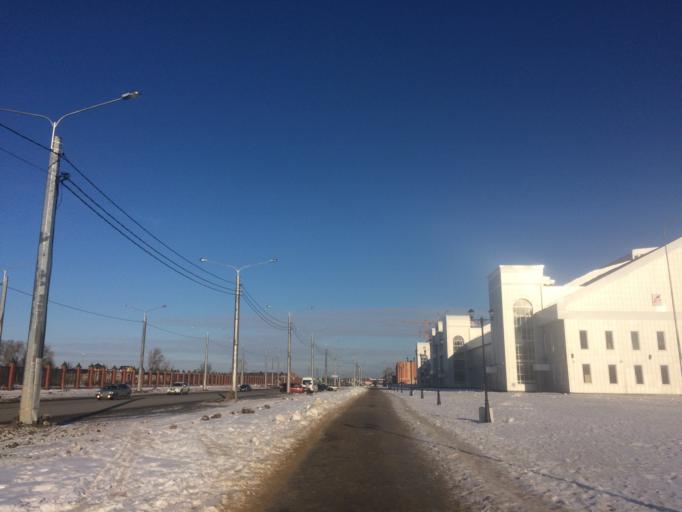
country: RU
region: Mariy-El
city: Yoshkar-Ola
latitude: 56.6385
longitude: 47.9142
